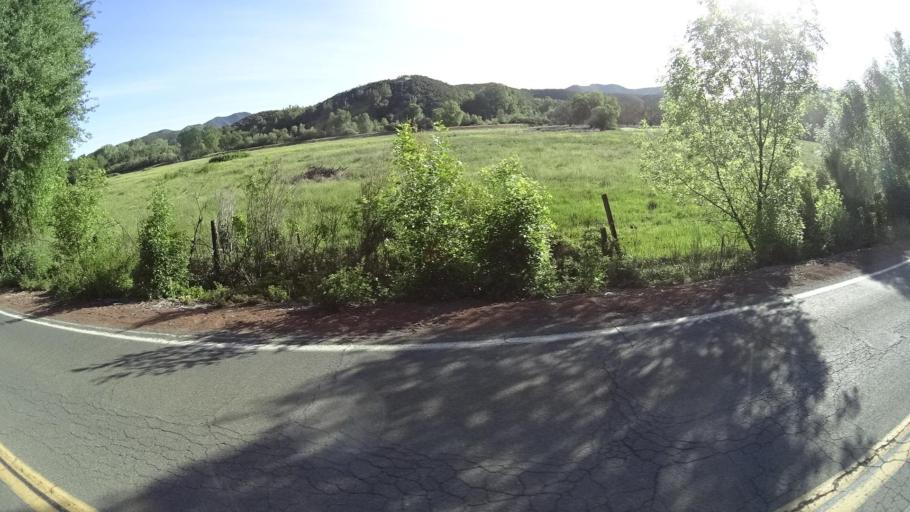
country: US
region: California
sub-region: Lake County
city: North Lakeport
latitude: 39.0915
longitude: -122.9582
